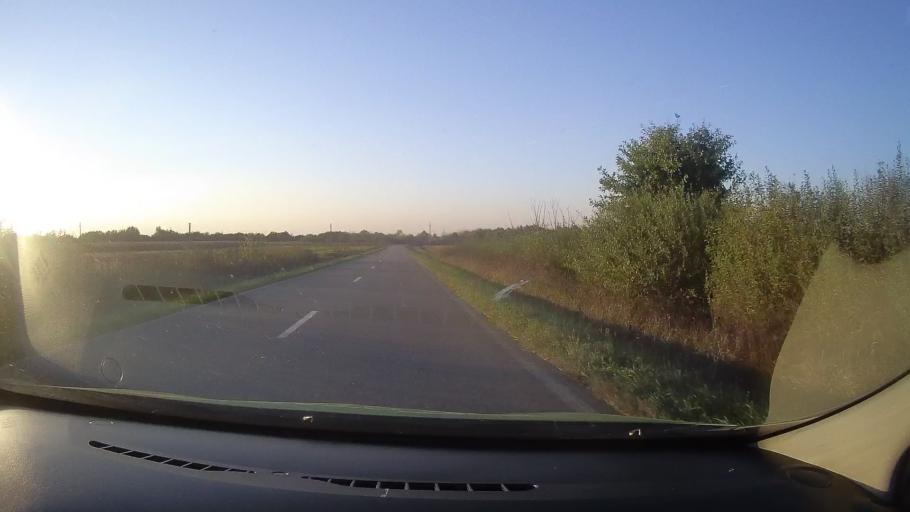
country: RO
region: Timis
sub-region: Comuna Traian Vuia
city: Traian Vuia
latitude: 45.7899
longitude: 22.0755
